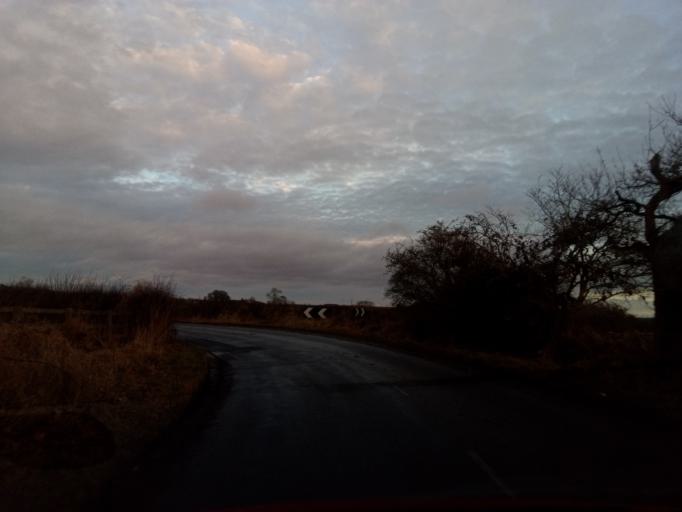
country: GB
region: England
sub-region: Northumberland
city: Ponteland
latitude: 55.0976
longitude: -1.7496
